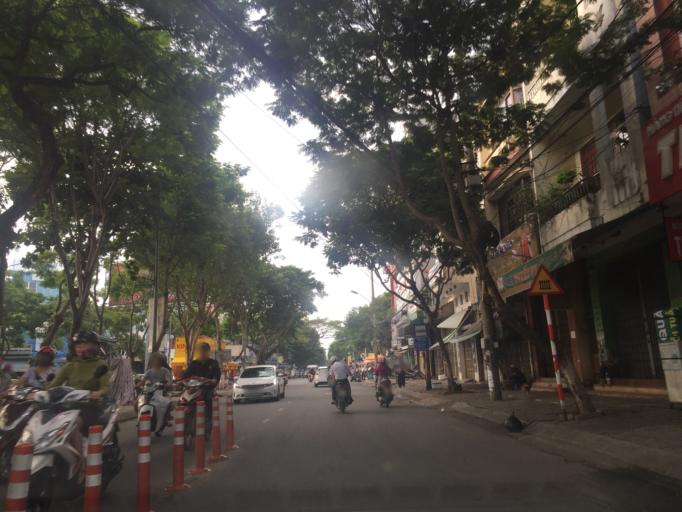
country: VN
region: Da Nang
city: Da Nang
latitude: 16.0732
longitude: 108.2129
